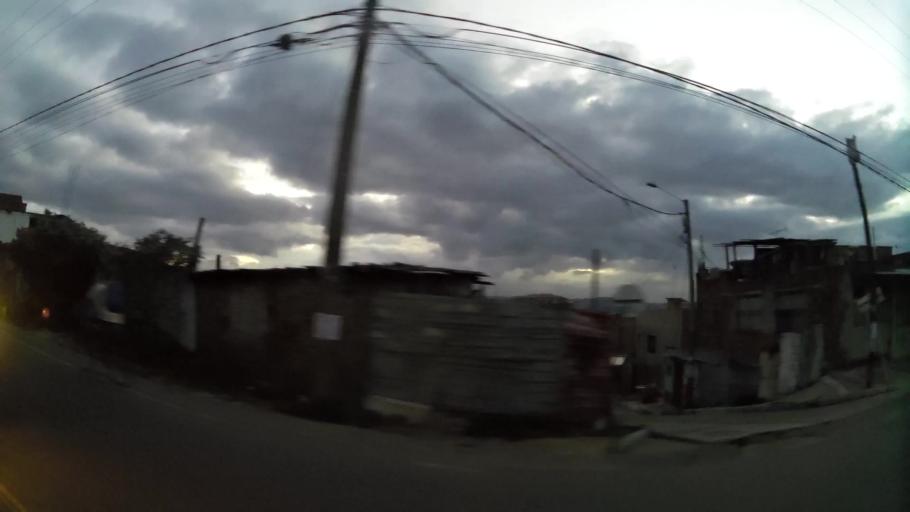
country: CO
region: Bogota D.C.
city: Bogota
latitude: 4.5479
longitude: -74.0838
